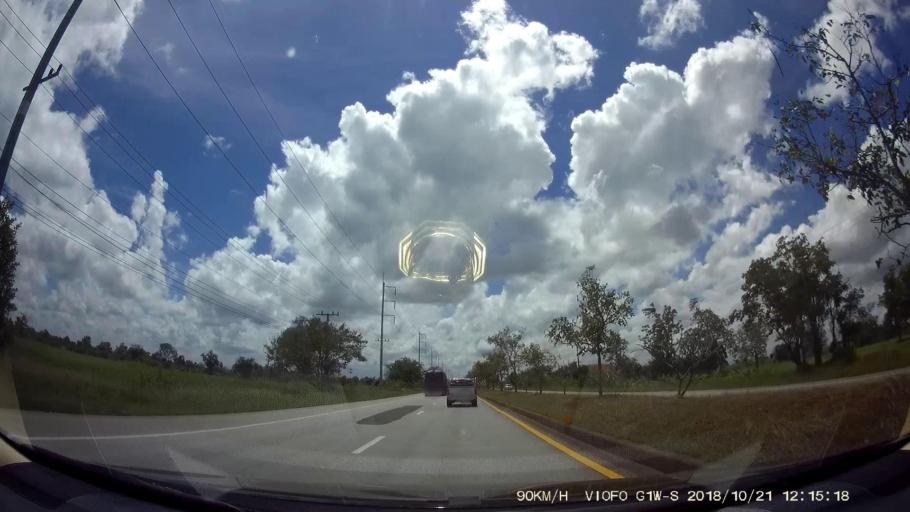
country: TH
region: Nakhon Ratchasima
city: Dan Khun Thot
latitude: 15.3646
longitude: 101.8311
